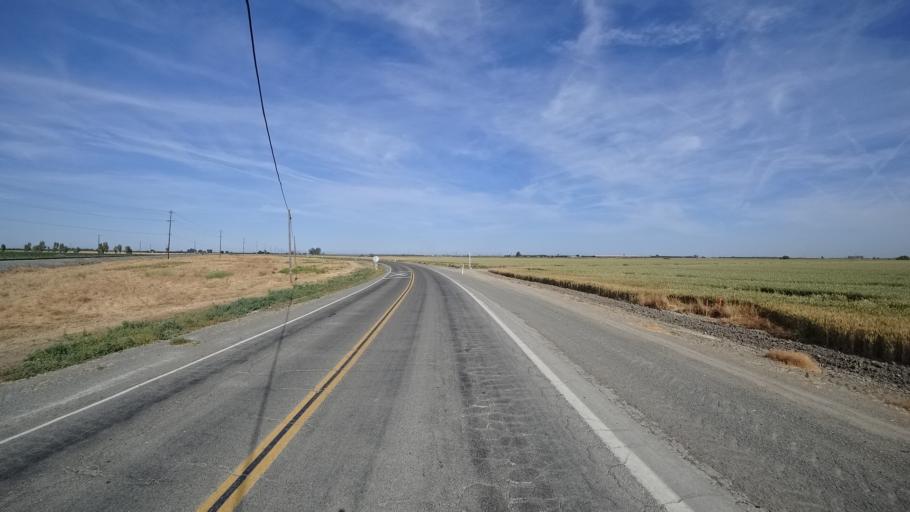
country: US
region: California
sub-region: Tulare County
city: Goshen
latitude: 36.3429
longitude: -119.5302
